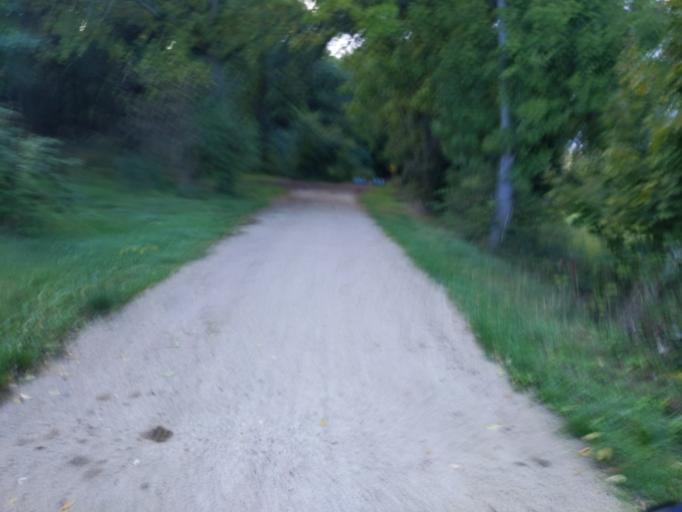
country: FR
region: Ile-de-France
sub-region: Departement des Yvelines
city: Saint-Remy-les-Chevreuse
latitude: 48.7010
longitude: 2.0935
